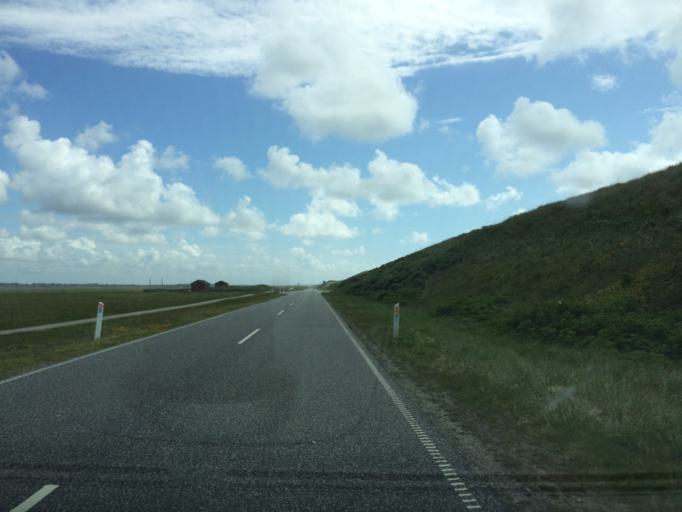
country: DK
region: Central Jutland
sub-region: Holstebro Kommune
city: Ulfborg
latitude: 56.3543
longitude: 8.1223
